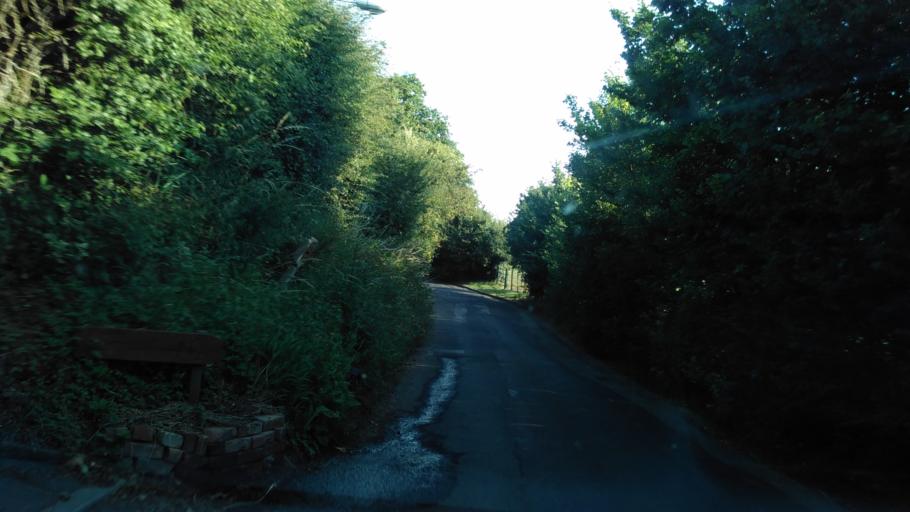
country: GB
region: England
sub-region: Kent
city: Whitstable
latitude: 51.3315
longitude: 1.0019
